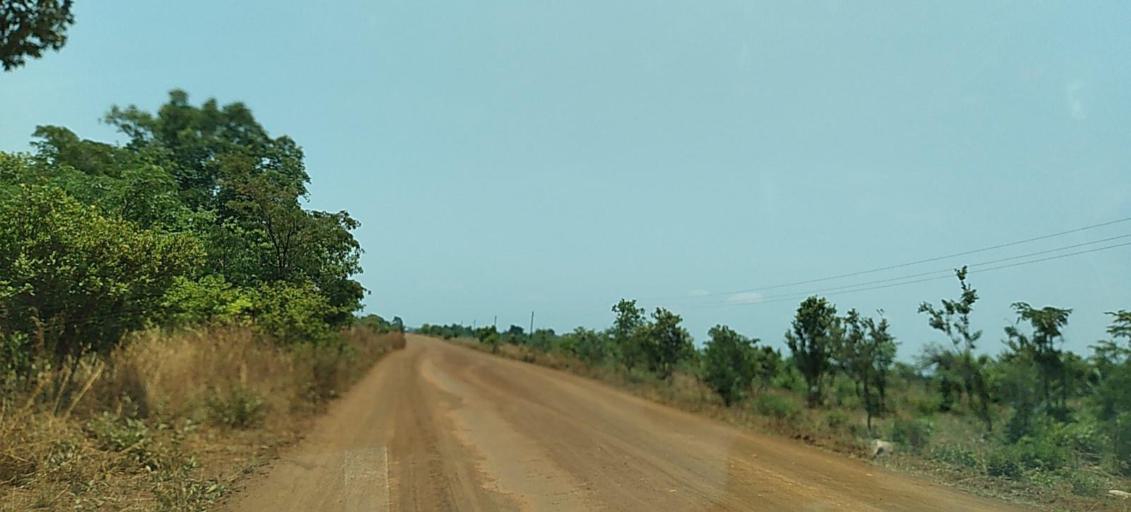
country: ZM
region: Copperbelt
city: Mpongwe
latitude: -13.6834
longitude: 27.8591
